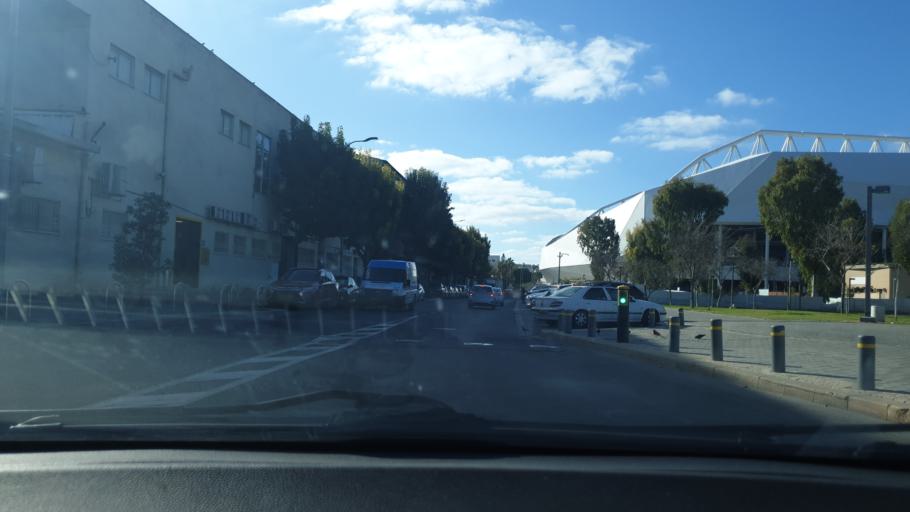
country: IL
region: Tel Aviv
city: Yafo
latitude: 32.0500
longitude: 34.7637
